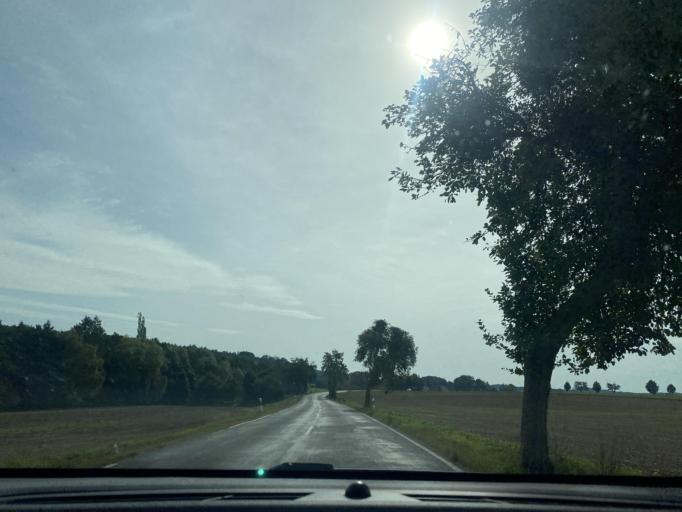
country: DE
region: Saxony
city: Reichenbach
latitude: 51.1808
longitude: 14.7690
